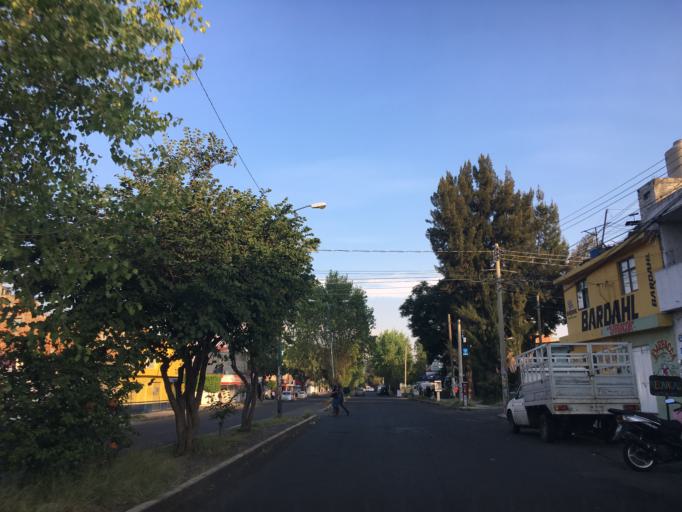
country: MX
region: Michoacan
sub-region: Tarimbaro
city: Real Hacienda (Metropolis)
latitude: 19.7210
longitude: -101.2206
